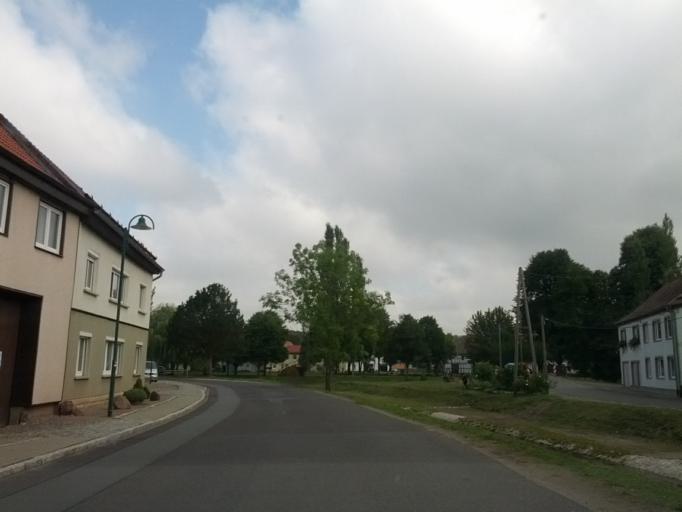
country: DE
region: Thuringia
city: Ernstroda
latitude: 50.9020
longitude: 10.6311
